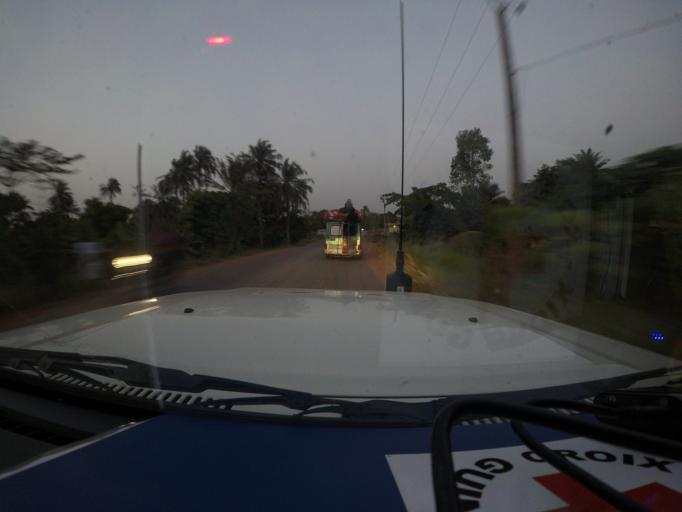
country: GN
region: Kindia
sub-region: Kindia
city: Kindia
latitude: 9.9577
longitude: -12.9444
